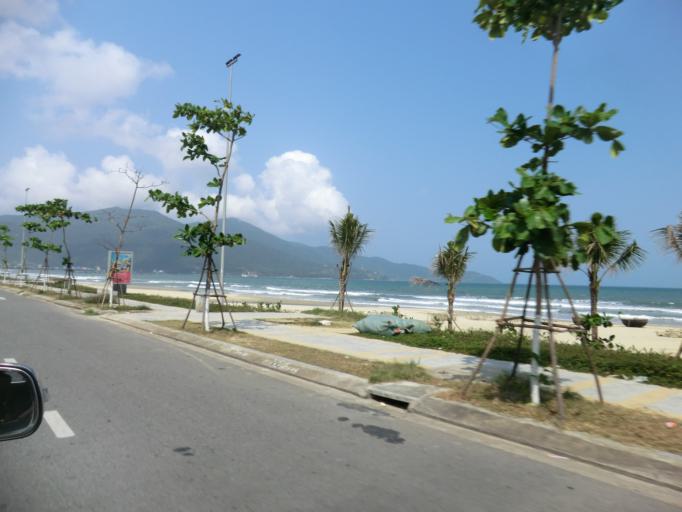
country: VN
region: Da Nang
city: Son Tra
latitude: 16.0817
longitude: 108.2475
